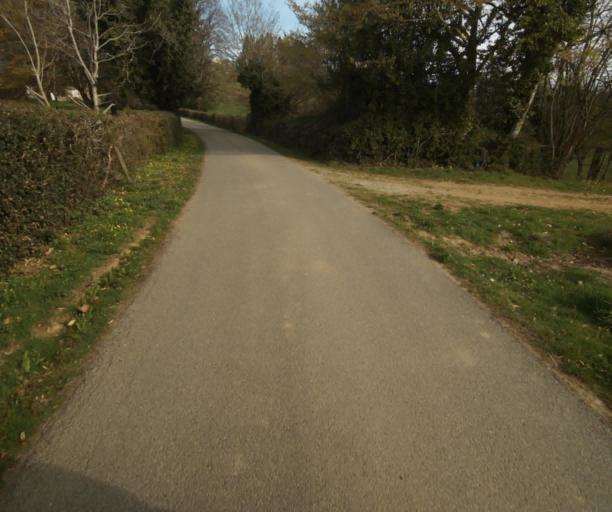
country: FR
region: Limousin
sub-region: Departement de la Correze
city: Chamboulive
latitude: 45.4205
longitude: 1.7893
